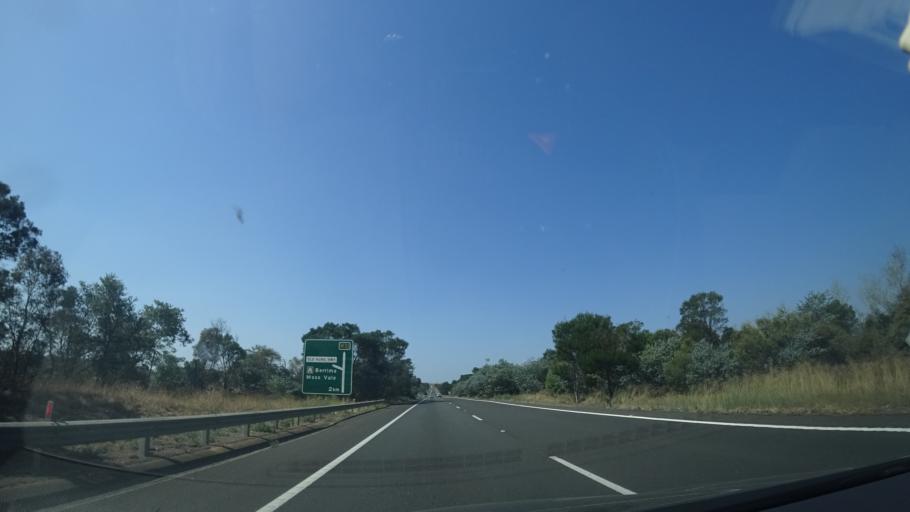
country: AU
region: New South Wales
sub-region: Wingecarribee
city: Moss Vale
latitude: -34.5339
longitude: 150.2835
